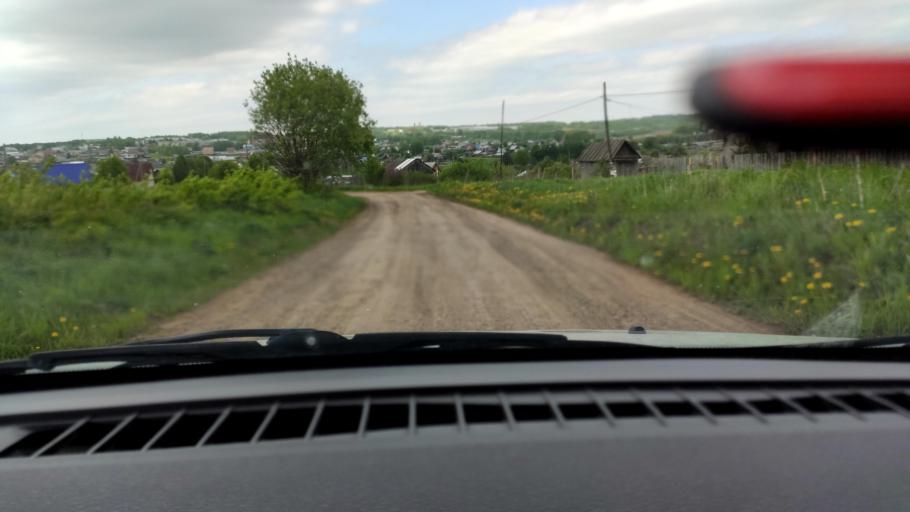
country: RU
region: Perm
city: Bershet'
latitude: 57.7259
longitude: 56.3884
